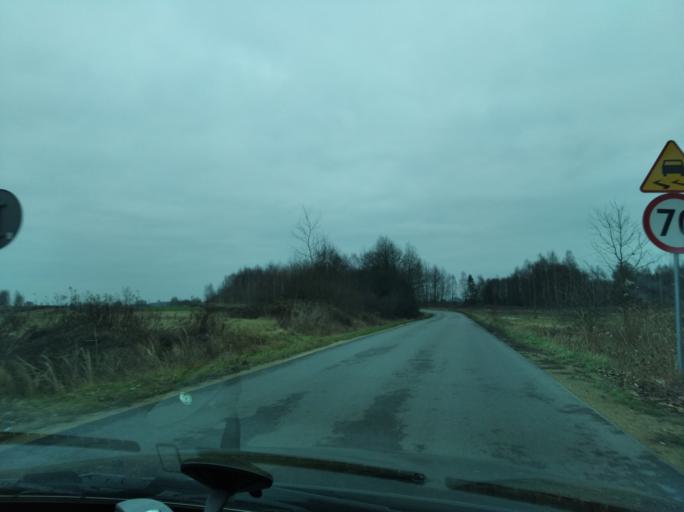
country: PL
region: Subcarpathian Voivodeship
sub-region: Powiat lancucki
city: Rakszawa
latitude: 50.1613
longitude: 22.2192
